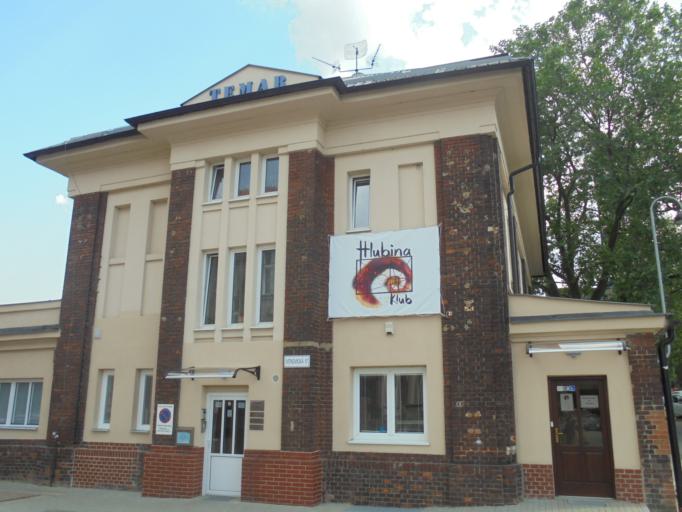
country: CZ
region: Moravskoslezsky
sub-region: Okres Ostrava-Mesto
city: Ostrava
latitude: 49.8216
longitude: 18.2732
